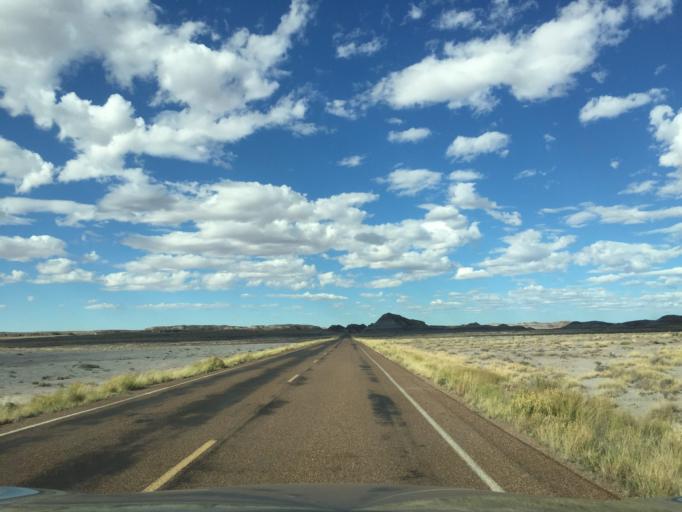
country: US
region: Arizona
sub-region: Navajo County
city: Holbrook
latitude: 34.9343
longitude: -109.7821
